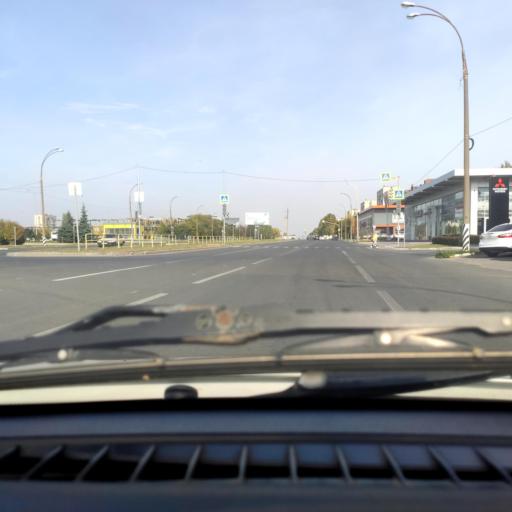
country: RU
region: Samara
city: Tol'yatti
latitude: 53.5003
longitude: 49.2748
